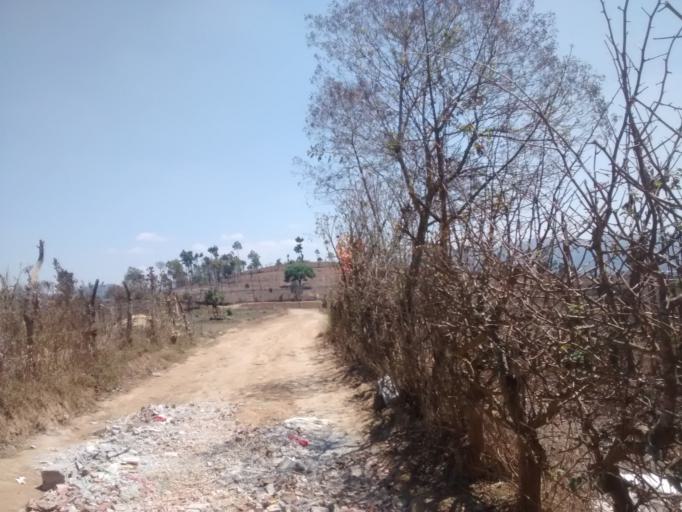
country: GT
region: Sacatepequez
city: Sumpango
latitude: 14.6683
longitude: -90.7337
